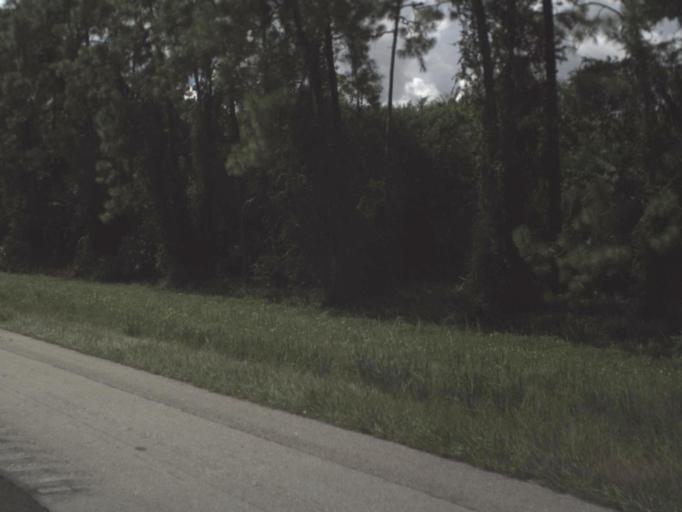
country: US
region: Florida
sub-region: Collier County
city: Vineyards
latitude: 26.2485
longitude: -81.7388
